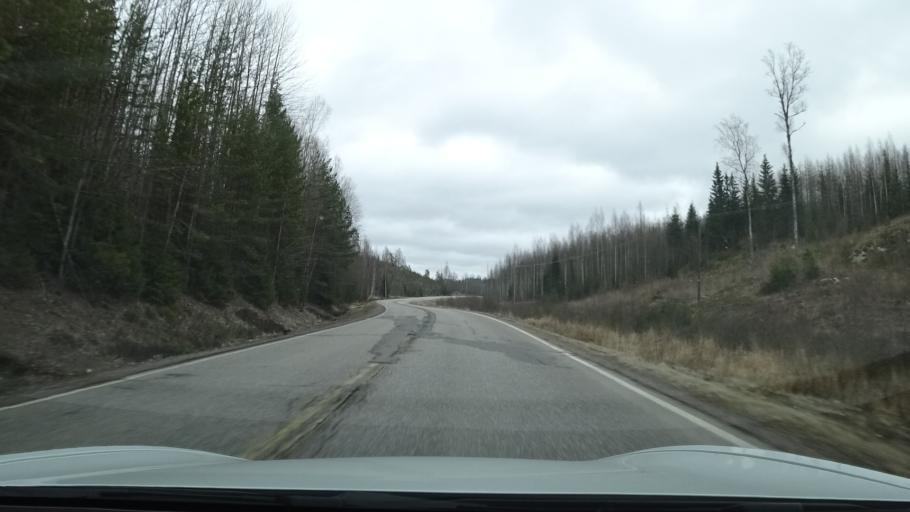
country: FI
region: Uusimaa
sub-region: Porvoo
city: Myrskylae
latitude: 60.6650
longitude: 25.7729
